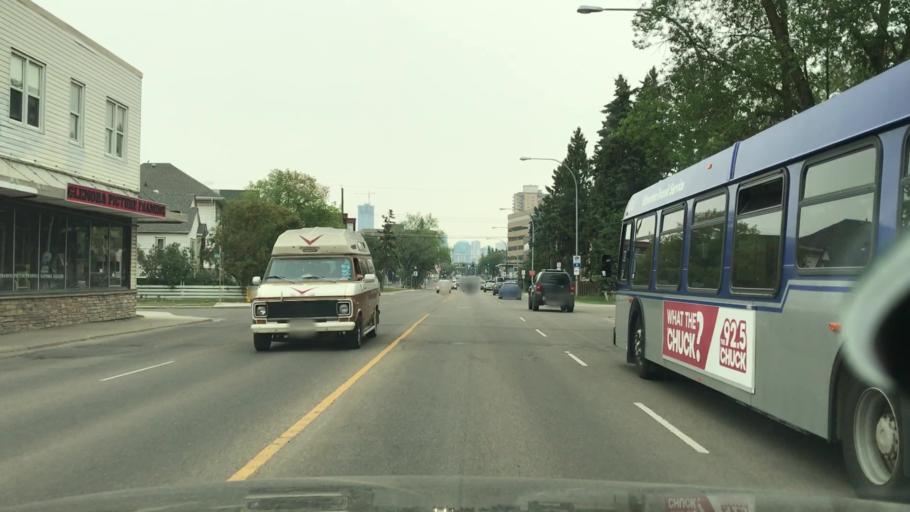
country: CA
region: Alberta
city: Edmonton
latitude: 53.5475
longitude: -113.5400
